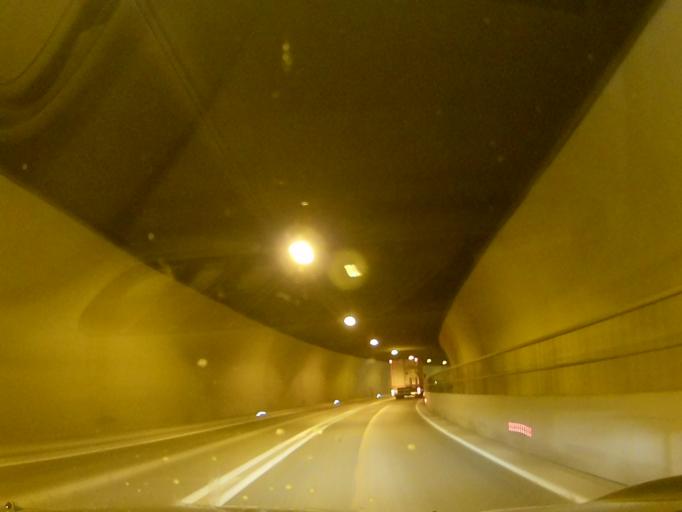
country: AT
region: Salzburg
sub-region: Politischer Bezirk Zell am See
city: Lend
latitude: 47.2881
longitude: 13.0634
